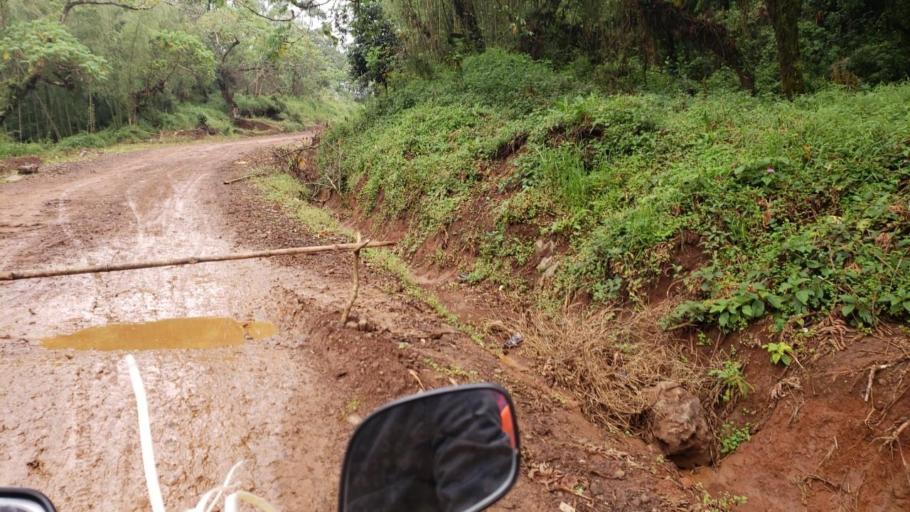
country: CD
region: South Kivu
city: Kabare
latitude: -2.2662
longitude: 28.6603
